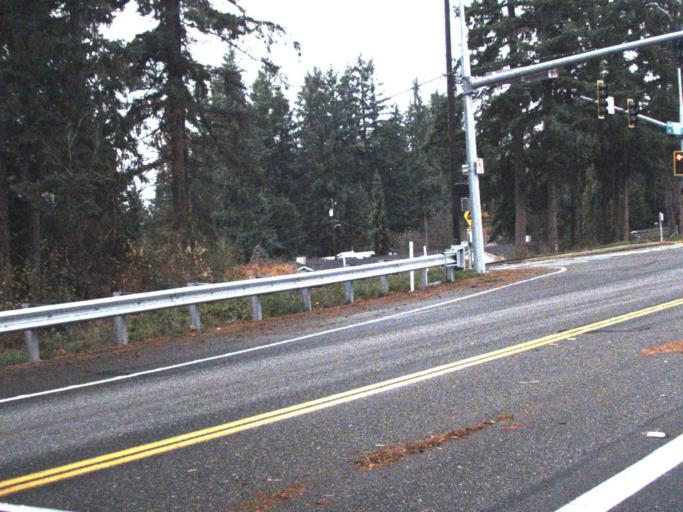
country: US
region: Washington
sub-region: Snohomish County
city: Fobes Hill
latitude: 47.9672
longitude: -122.1022
